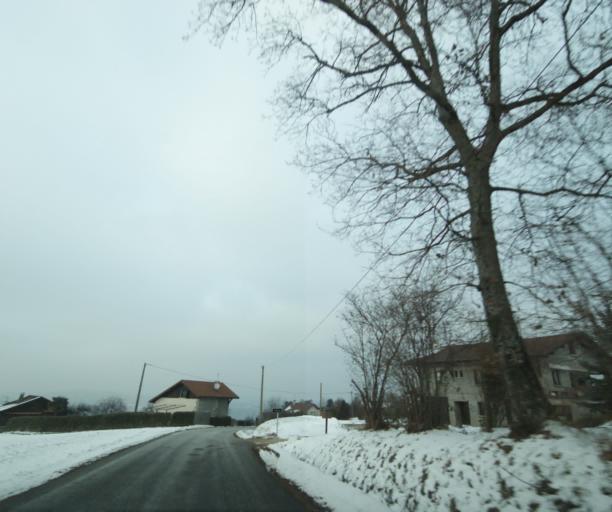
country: FR
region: Rhone-Alpes
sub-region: Departement de la Haute-Savoie
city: Reignier-Esery
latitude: 46.1328
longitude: 6.2450
